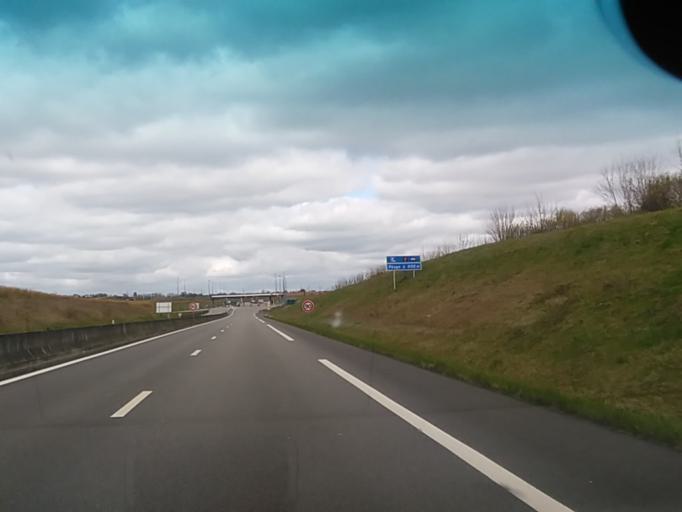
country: FR
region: Haute-Normandie
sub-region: Departement de l'Eure
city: Bourg-Achard
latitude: 49.3497
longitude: 0.8353
